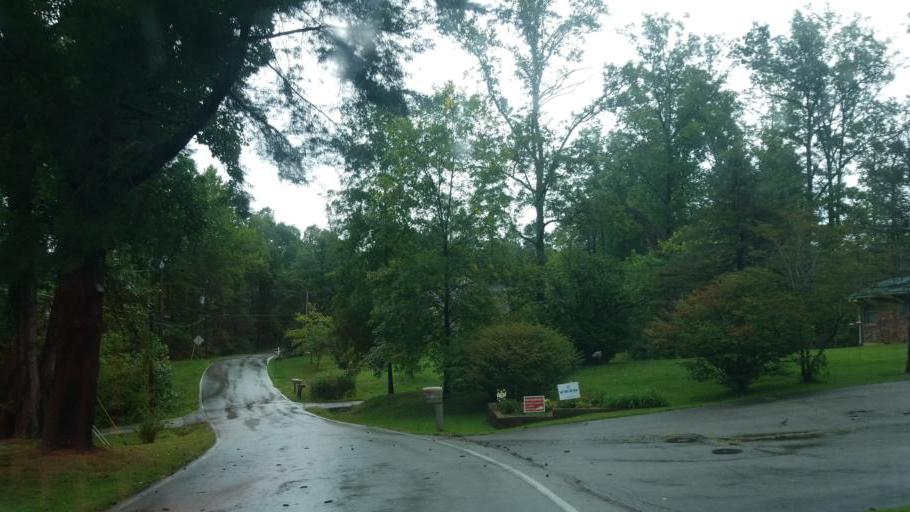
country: US
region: Kentucky
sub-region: Rowan County
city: Morehead
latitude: 38.1795
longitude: -83.4860
